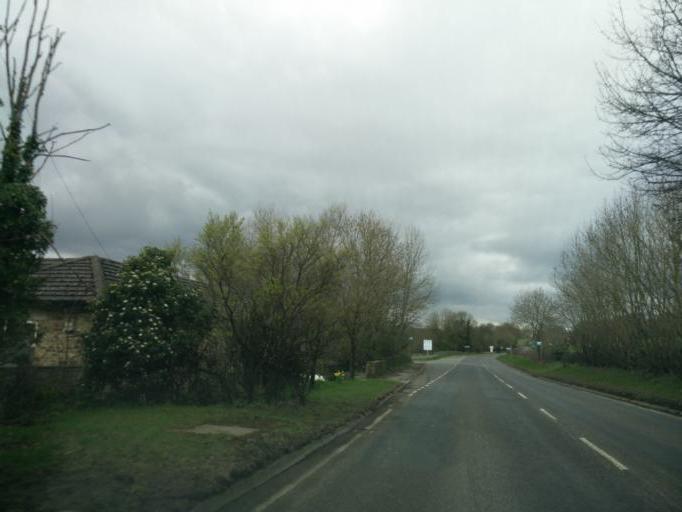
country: GB
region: England
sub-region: County Durham
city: Wolsingham
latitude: 54.7274
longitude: -1.9453
